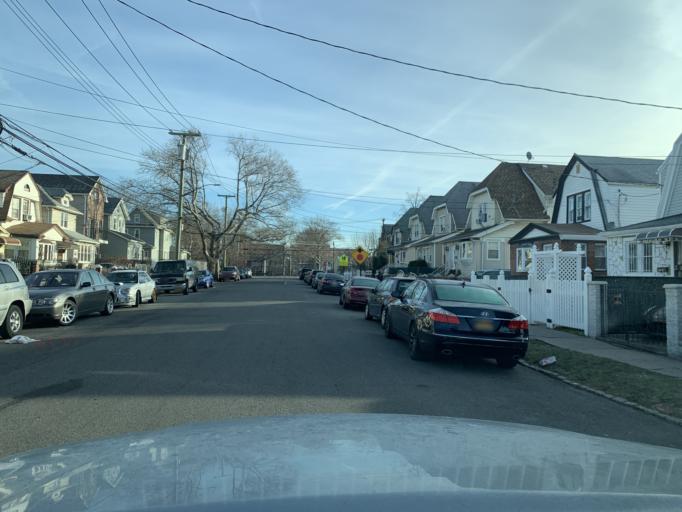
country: US
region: New York
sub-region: Queens County
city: Jamaica
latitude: 40.6959
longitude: -73.7878
